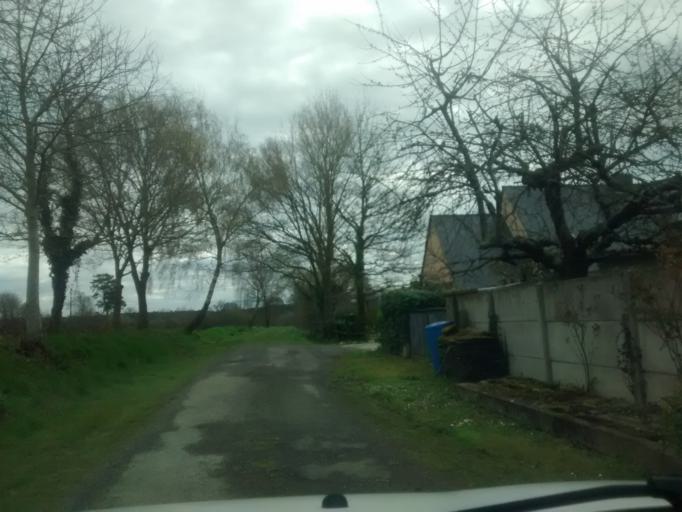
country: FR
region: Brittany
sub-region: Departement d'Ille-et-Vilaine
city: Saint-Sulpice-la-Foret
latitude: 48.2253
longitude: -1.5693
